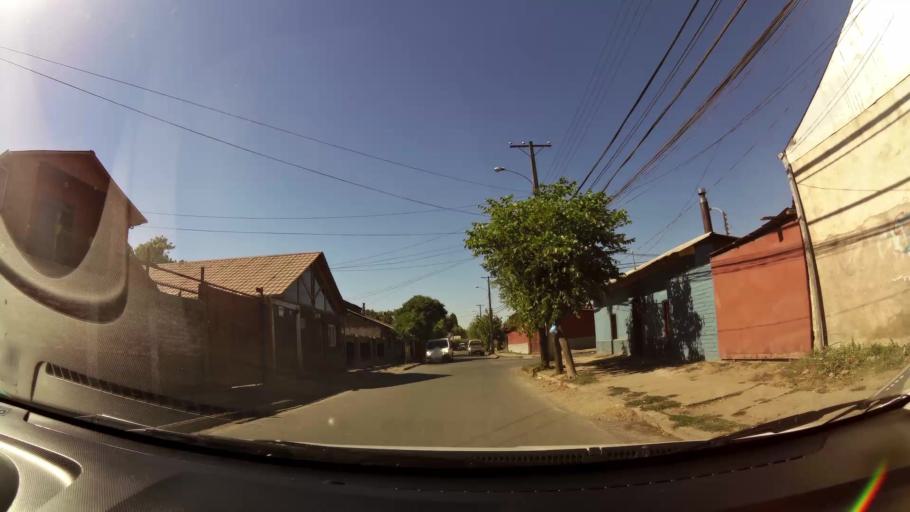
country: CL
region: O'Higgins
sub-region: Provincia de Colchagua
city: Chimbarongo
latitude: -34.5875
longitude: -70.9990
